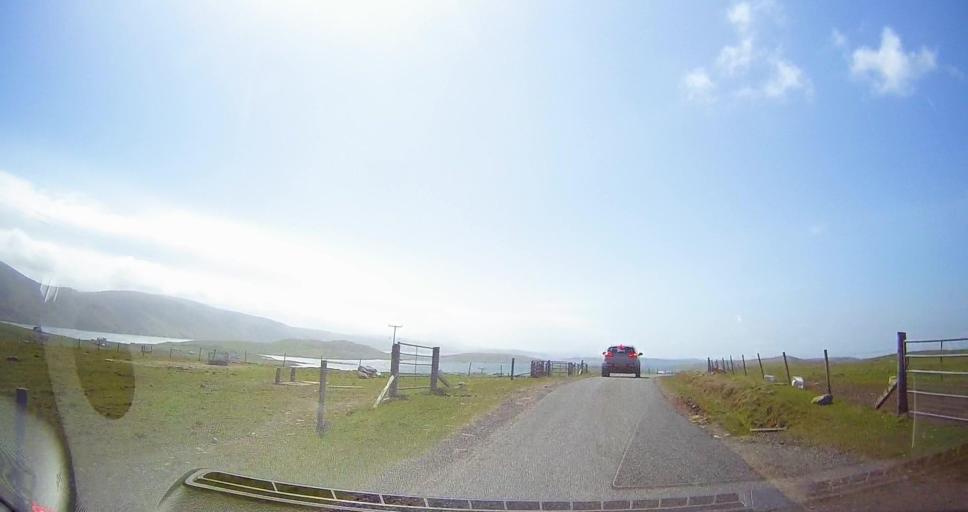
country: GB
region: Scotland
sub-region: Shetland Islands
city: Sandwick
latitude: 60.0749
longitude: -1.3383
